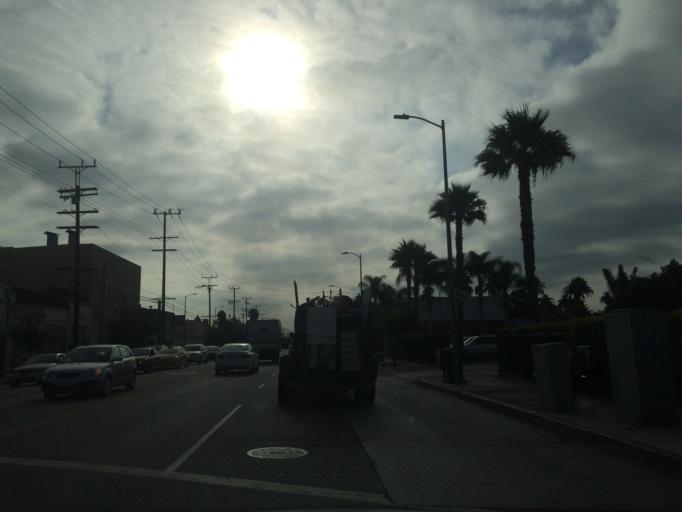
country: US
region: California
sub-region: Los Angeles County
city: View Park-Windsor Hills
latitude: 34.0325
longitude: -118.3563
